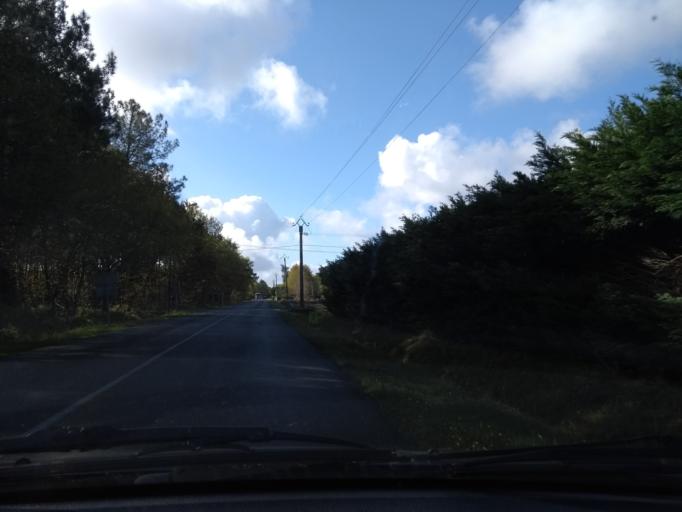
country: FR
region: Aquitaine
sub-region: Departement des Landes
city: Sanguinet
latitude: 44.4730
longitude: -1.0703
